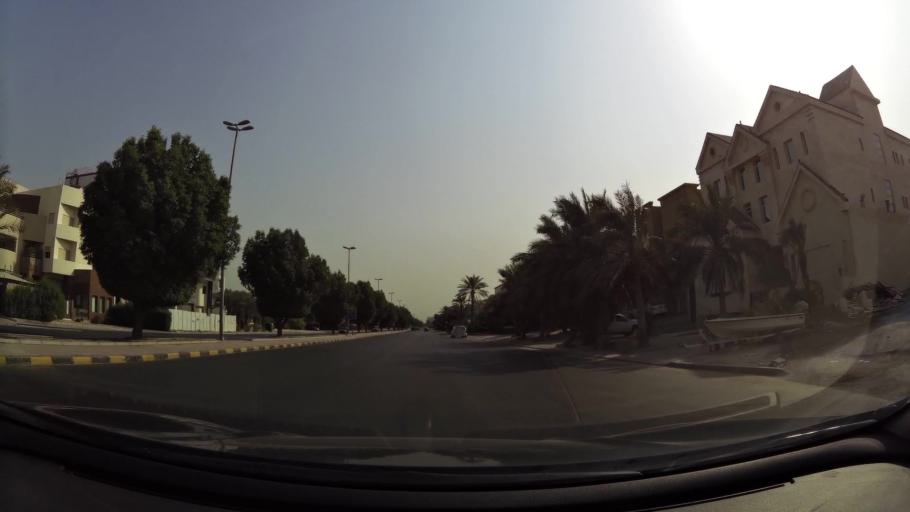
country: KW
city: Bayan
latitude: 29.2844
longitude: 48.0517
